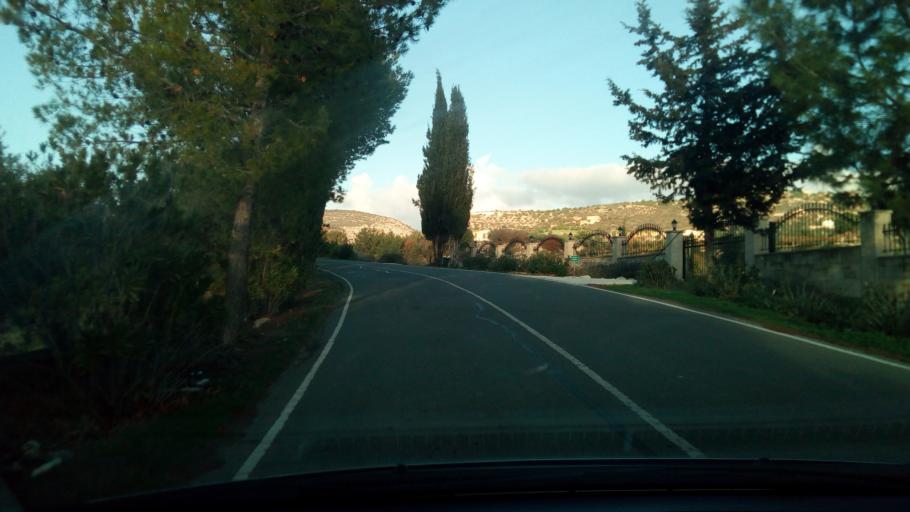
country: CY
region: Pafos
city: Polis
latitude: 34.9851
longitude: 32.4707
